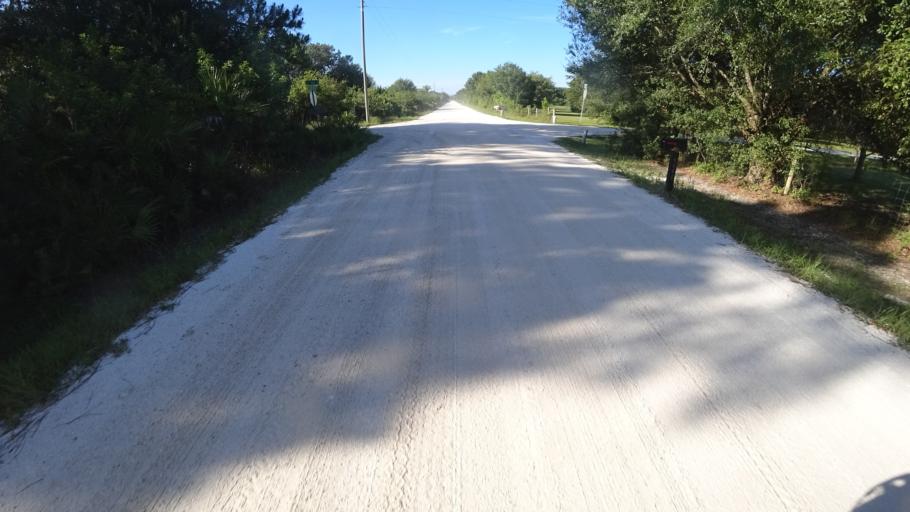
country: US
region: Florida
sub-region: Sarasota County
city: The Meadows
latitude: 27.4195
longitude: -82.2614
